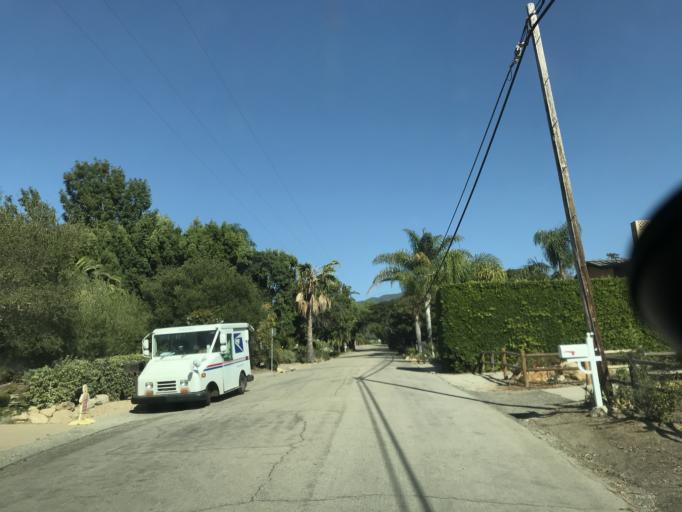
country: US
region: California
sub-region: Santa Barbara County
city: Goleta
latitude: 34.4538
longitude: -119.7861
